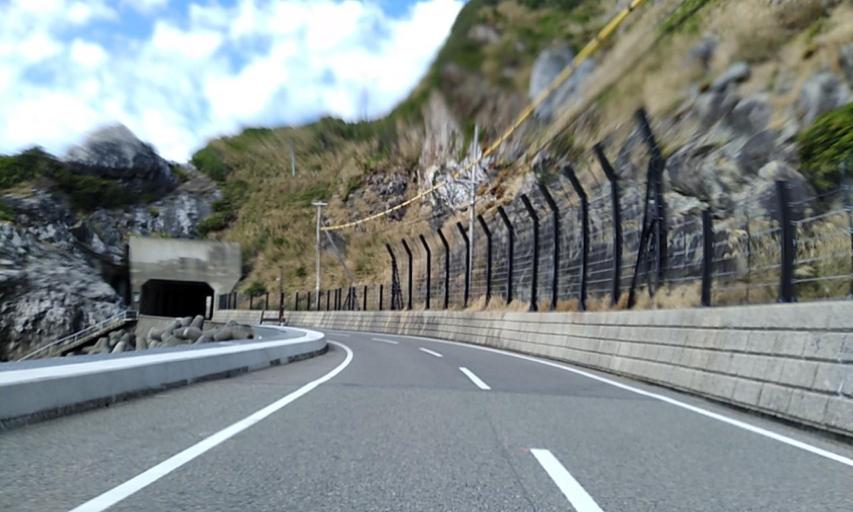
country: JP
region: Wakayama
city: Gobo
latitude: 33.9766
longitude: 135.0742
